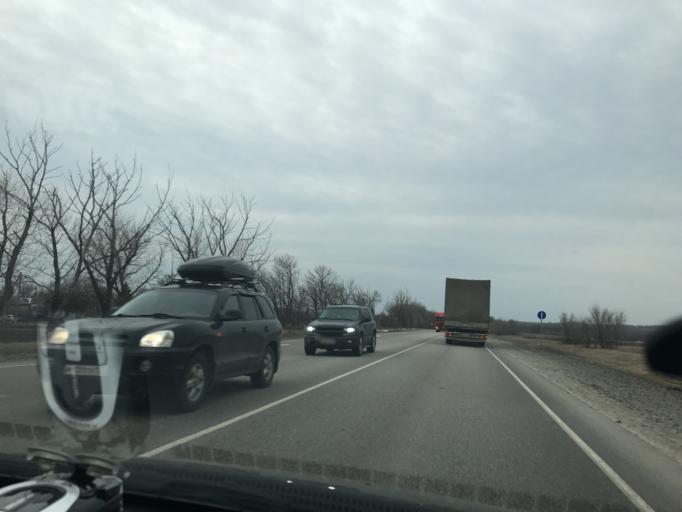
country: RU
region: Krasnodarskiy
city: Alekseyevskaya
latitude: 45.7047
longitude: 40.2921
